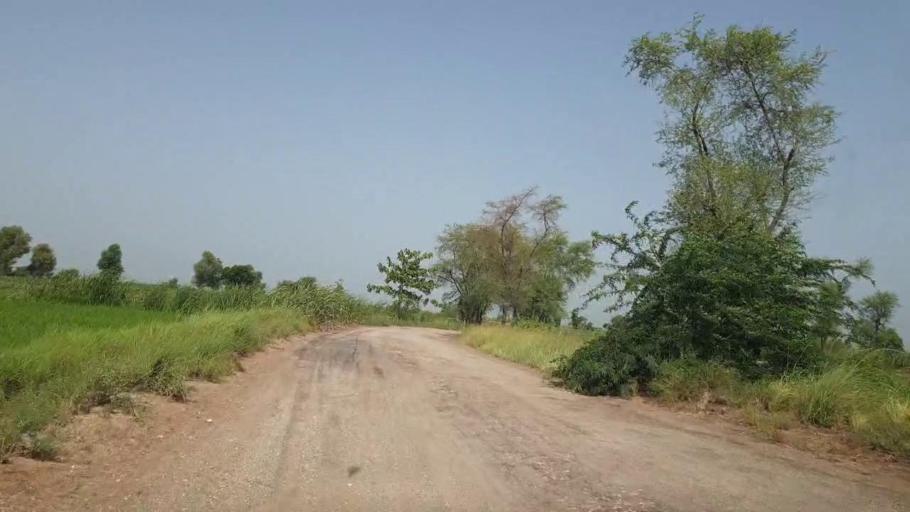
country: PK
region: Sindh
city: Sakrand
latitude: 26.2917
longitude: 68.2219
